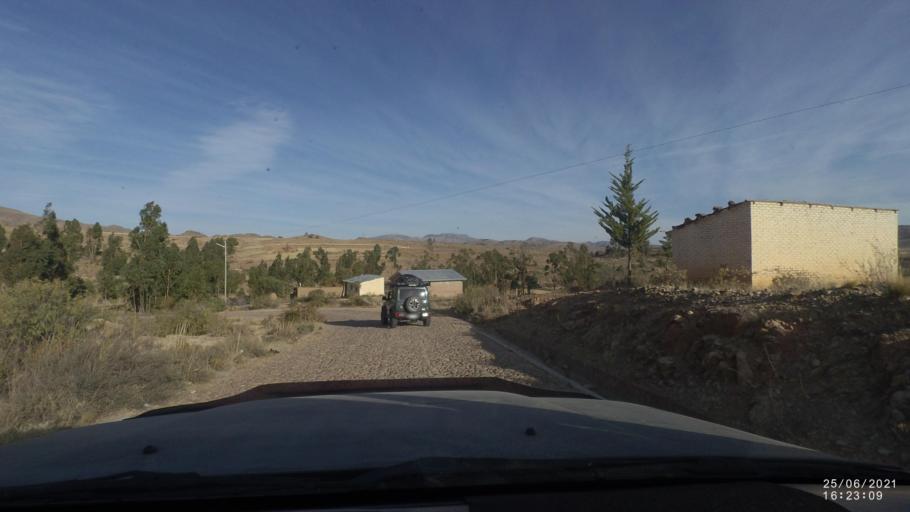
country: BO
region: Cochabamba
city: Cliza
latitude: -17.7591
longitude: -65.8320
